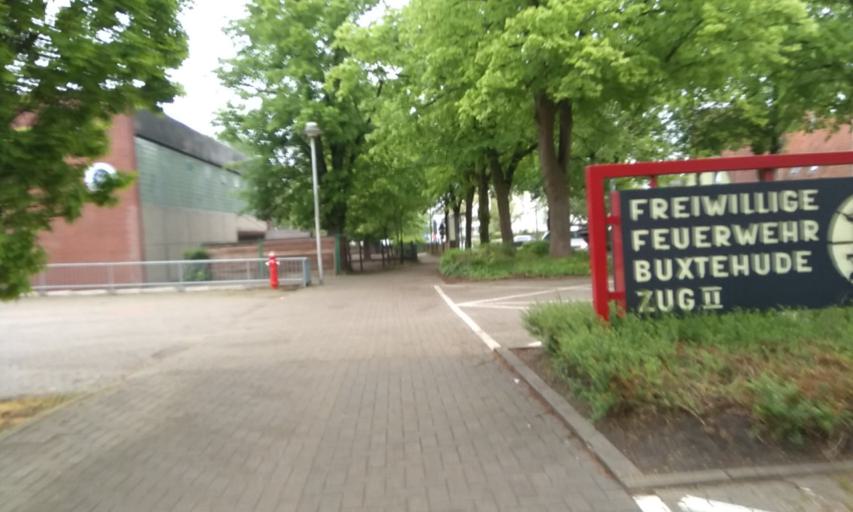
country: DE
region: Lower Saxony
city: Buxtehude
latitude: 53.4659
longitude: 9.6874
